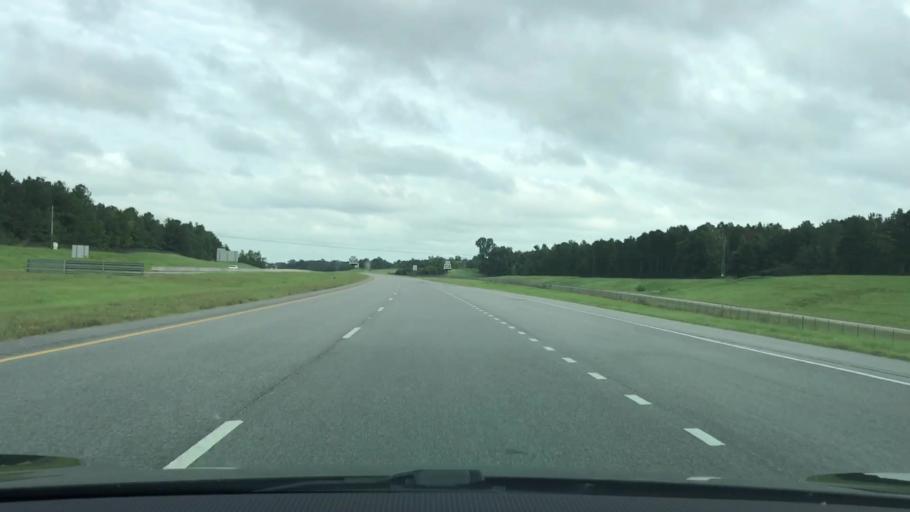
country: US
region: Alabama
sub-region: Montgomery County
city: Pike Road
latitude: 32.3431
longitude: -86.0637
